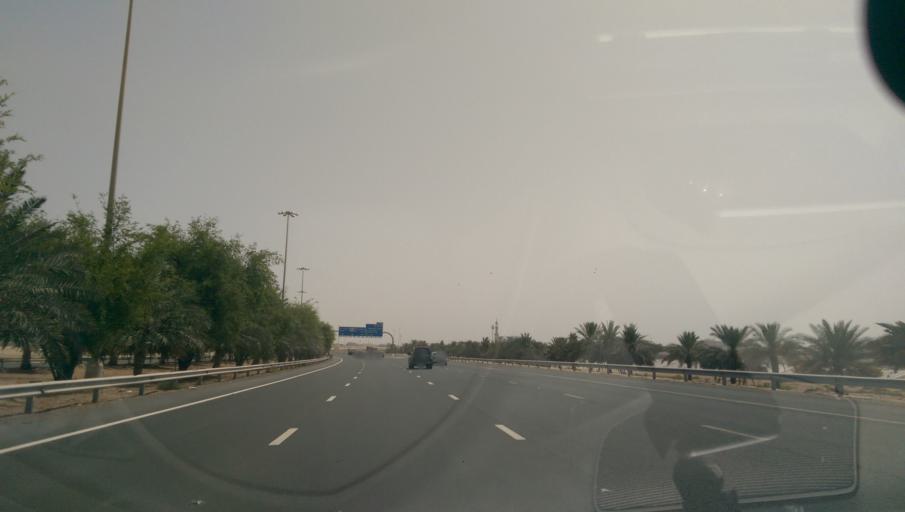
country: AE
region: Abu Dhabi
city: Abu Dhabi
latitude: 24.3325
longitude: 54.6311
